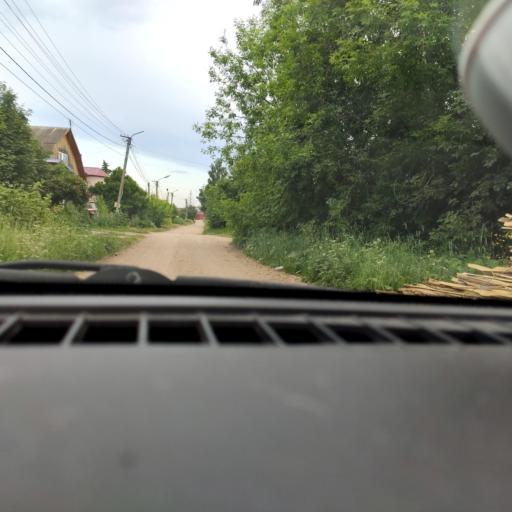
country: RU
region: Perm
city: Overyata
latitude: 58.0606
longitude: 55.8134
